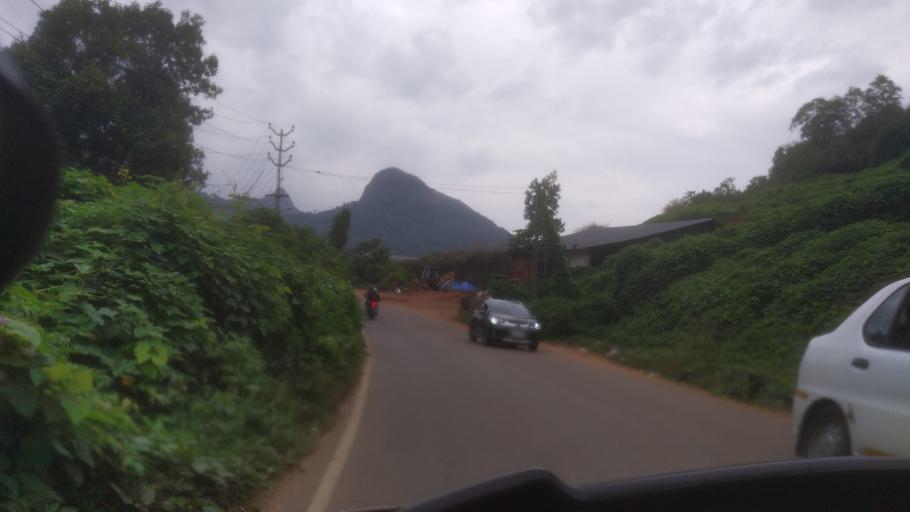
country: IN
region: Kerala
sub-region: Idukki
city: Munnar
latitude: 10.0070
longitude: 76.9611
